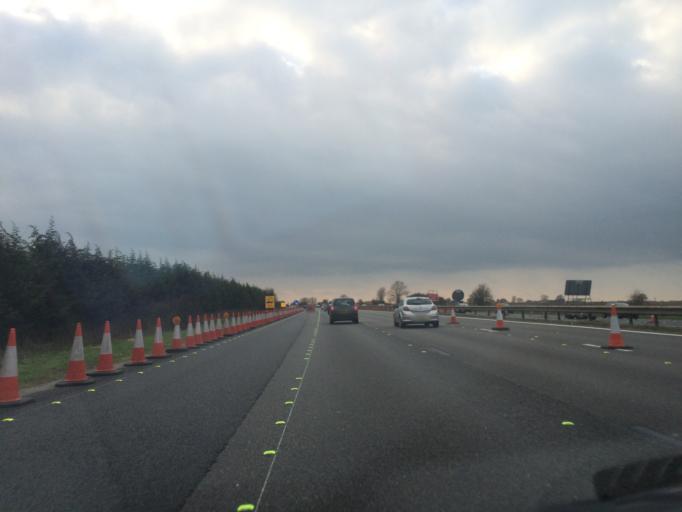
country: GB
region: England
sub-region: West Berkshire
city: Winterbourne
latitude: 51.4563
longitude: -1.3522
